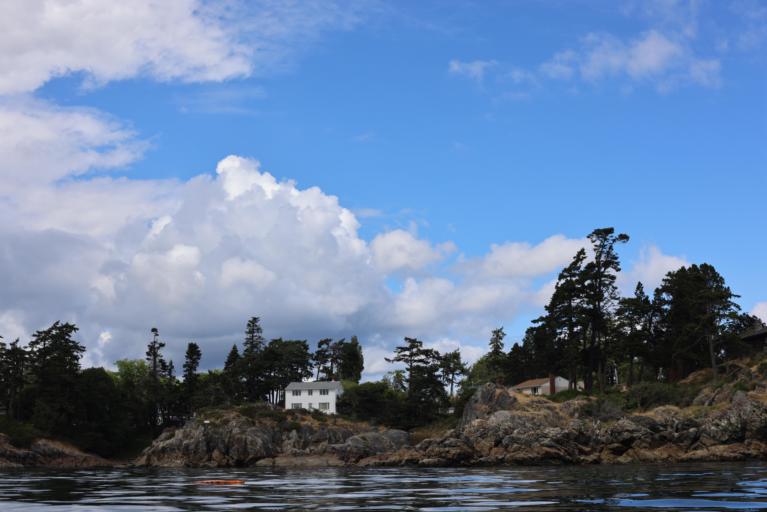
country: CA
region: British Columbia
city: Victoria
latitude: 48.4244
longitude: -123.4257
